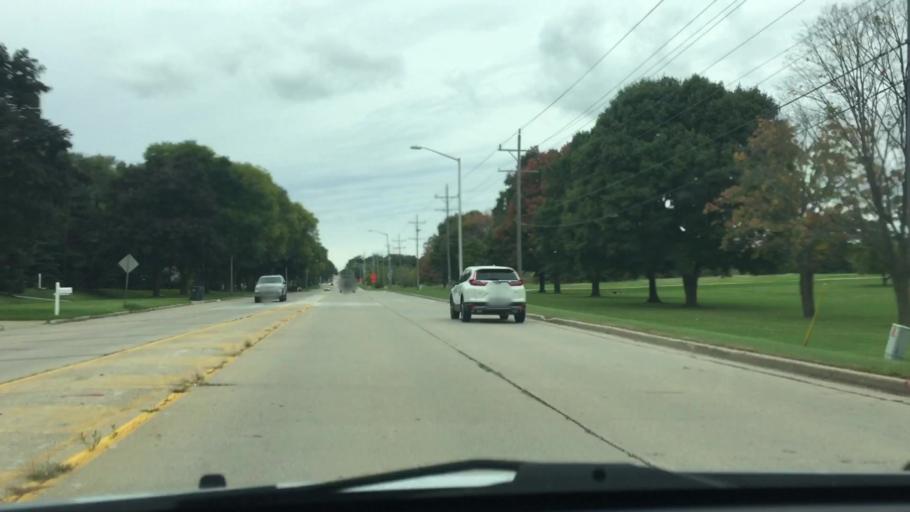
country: US
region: Wisconsin
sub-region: Waukesha County
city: Waukesha
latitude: 43.0323
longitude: -88.2473
